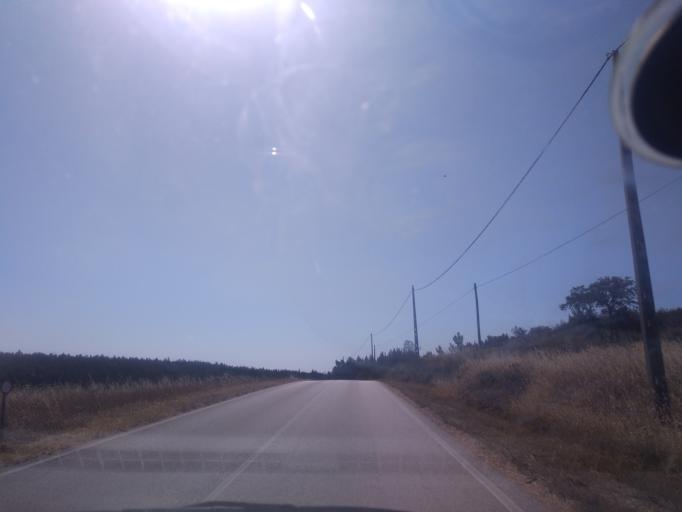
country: PT
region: Faro
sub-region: Aljezur
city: Aljezur
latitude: 37.2199
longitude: -8.7967
